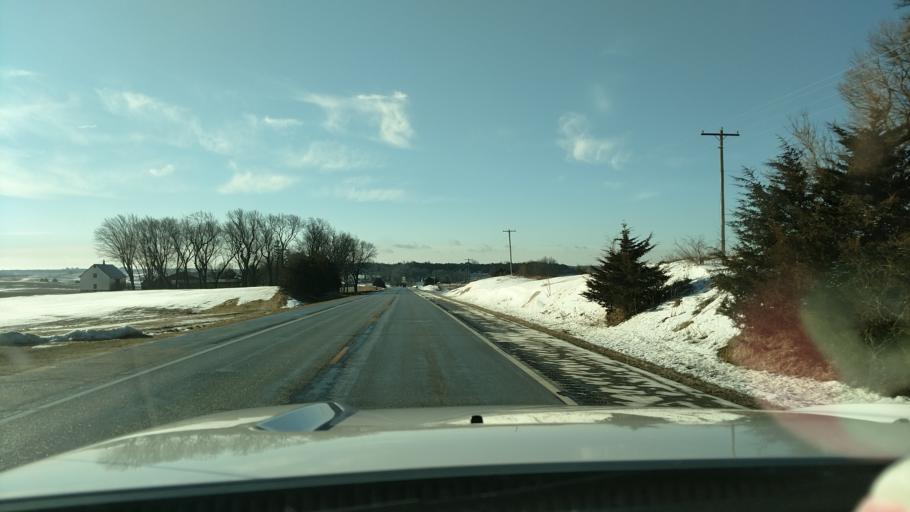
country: US
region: Minnesota
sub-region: Olmsted County
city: Oronoco
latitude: 44.1569
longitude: -92.4193
